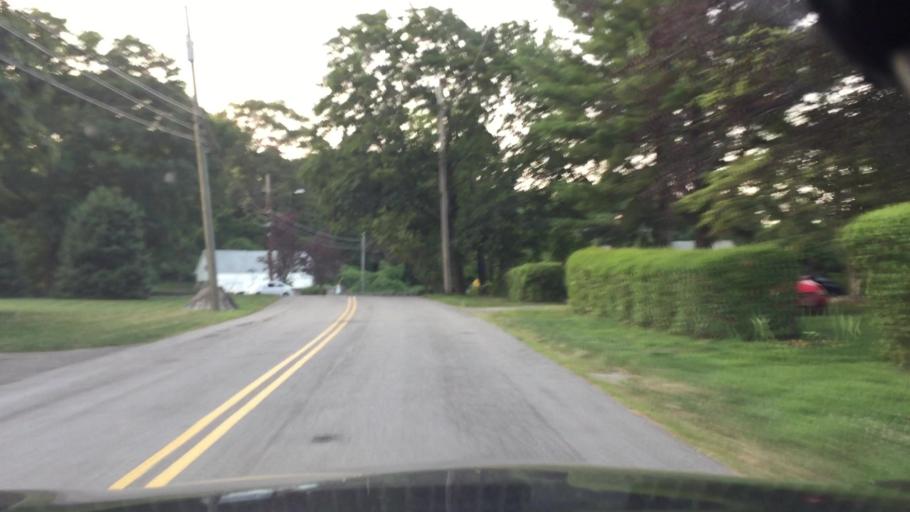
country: US
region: Connecticut
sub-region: Fairfield County
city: Fairfield
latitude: 41.1554
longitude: -73.2503
